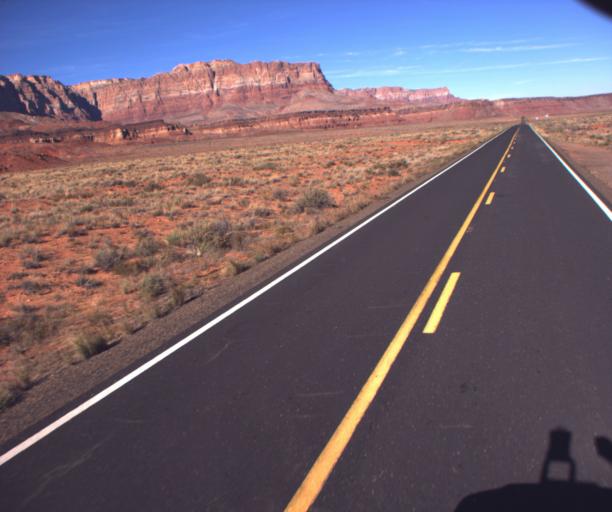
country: US
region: Arizona
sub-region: Coconino County
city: LeChee
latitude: 36.7179
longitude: -111.7731
